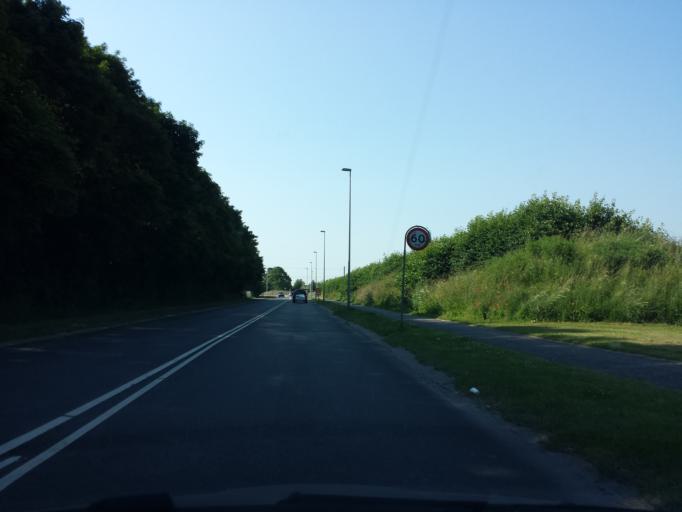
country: DK
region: Capital Region
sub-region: Egedal Kommune
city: Smorumnedre
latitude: 55.7316
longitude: 12.3098
